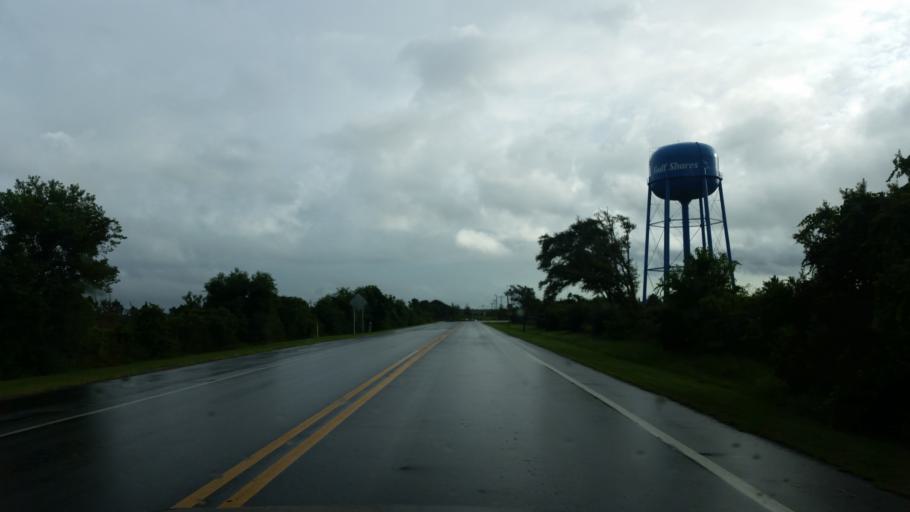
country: US
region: Alabama
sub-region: Baldwin County
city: Gulf Shores
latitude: 30.2574
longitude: -87.6529
